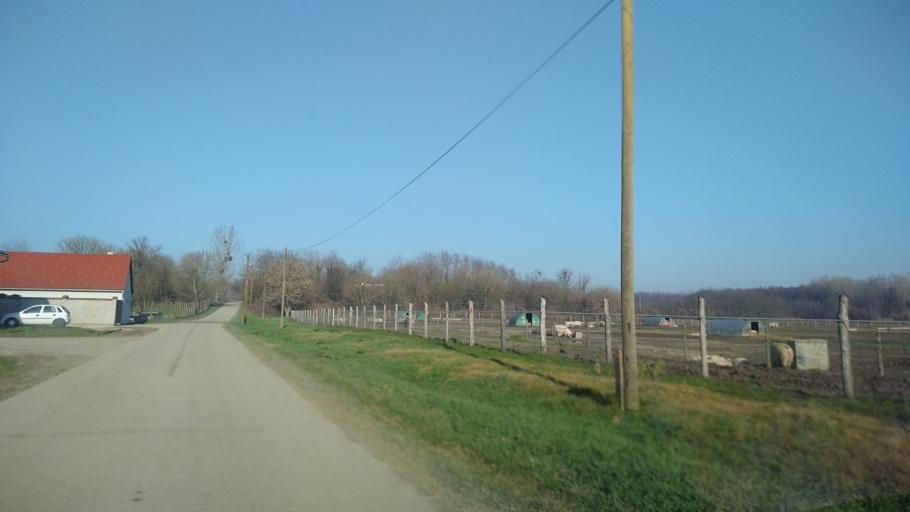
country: HU
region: Somogy
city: Barcs
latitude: 45.9526
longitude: 17.4878
